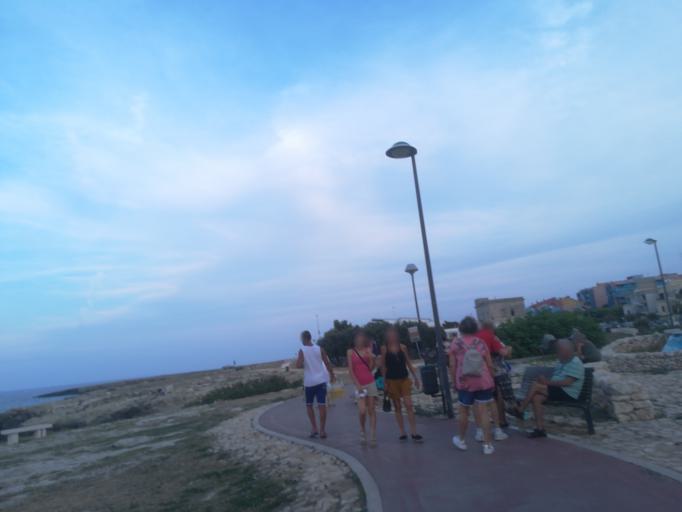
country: IT
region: Apulia
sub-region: Provincia di Bari
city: Monopoli
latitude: 40.9473
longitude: 17.3074
